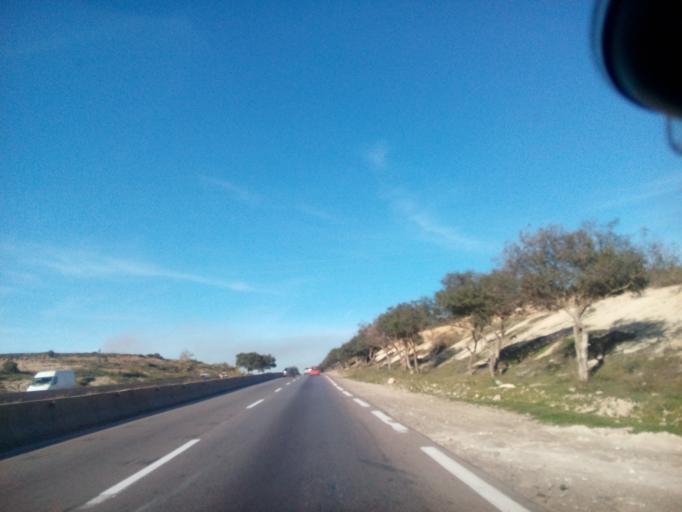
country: DZ
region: Oran
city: Ain el Bya
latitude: 35.7713
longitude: -0.2417
